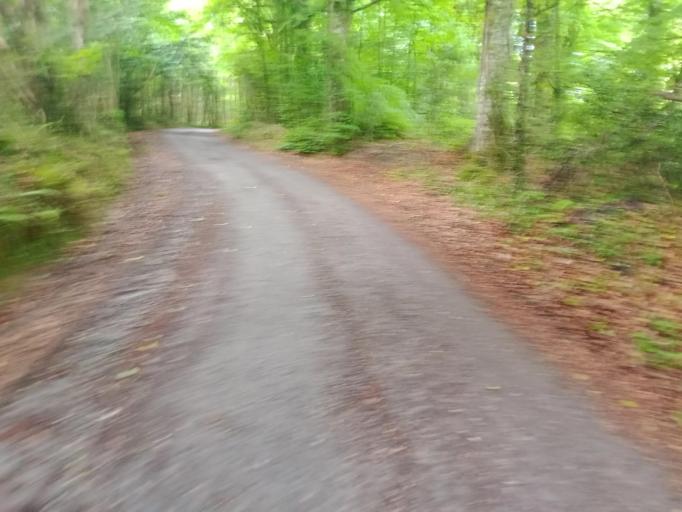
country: IE
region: Leinster
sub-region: Kilkenny
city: Thomastown
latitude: 52.4762
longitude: -7.0550
